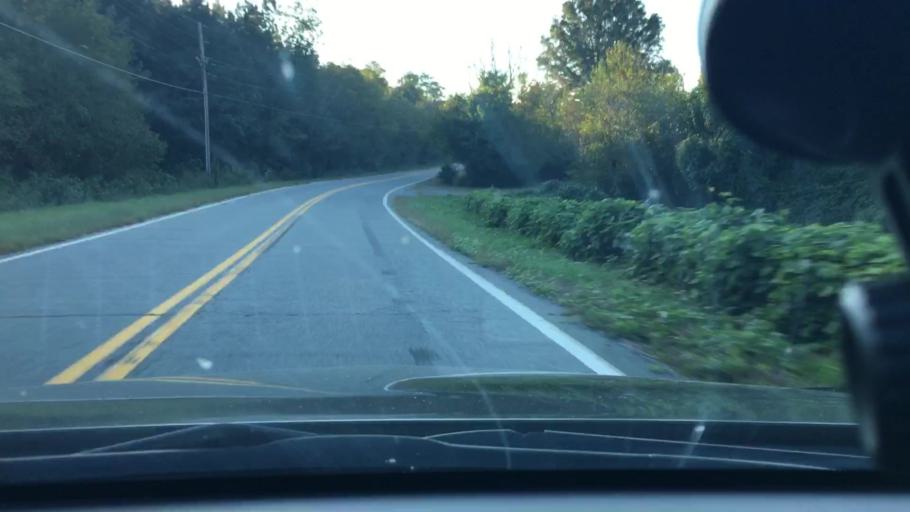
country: US
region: North Carolina
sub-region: Rutherford County
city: Rutherfordton
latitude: 35.3310
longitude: -82.0323
